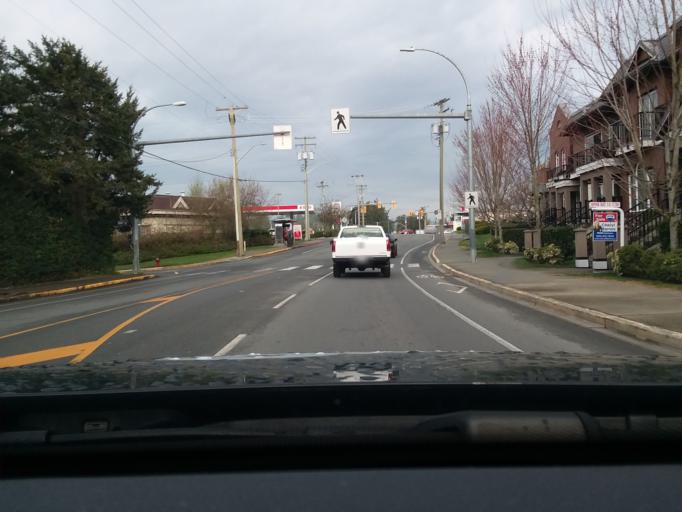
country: CA
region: British Columbia
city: Victoria
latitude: 48.4412
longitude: -123.4006
